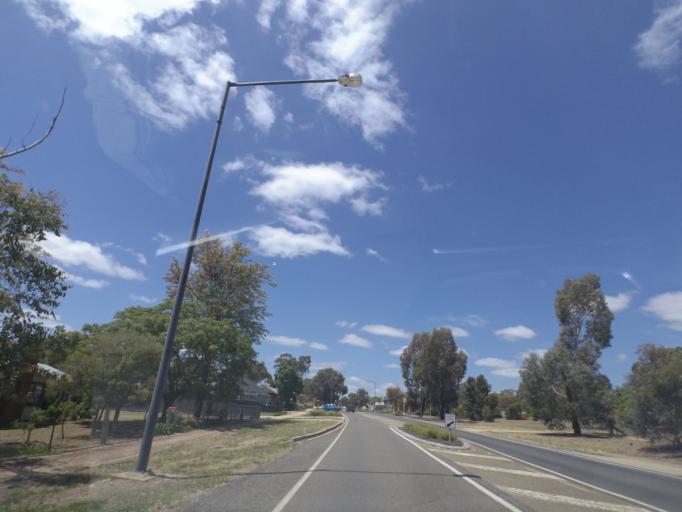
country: AU
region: Victoria
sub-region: Wangaratta
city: Wangaratta
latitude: -36.4642
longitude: 146.2201
